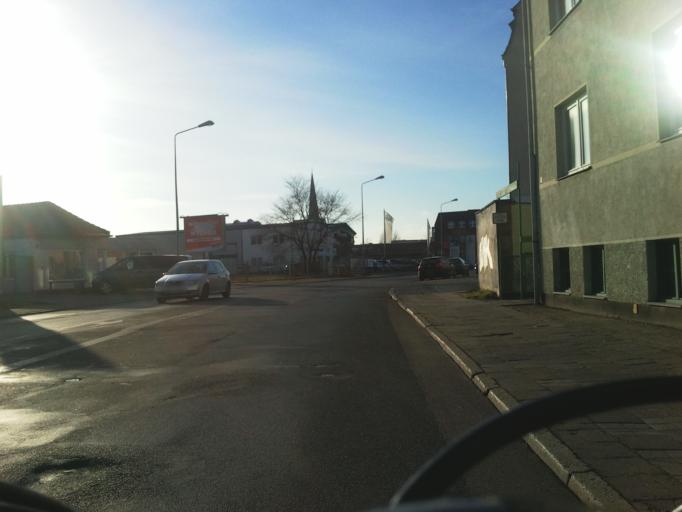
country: DE
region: Mecklenburg-Vorpommern
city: Dierkow-Neu
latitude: 54.0916
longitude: 12.1607
